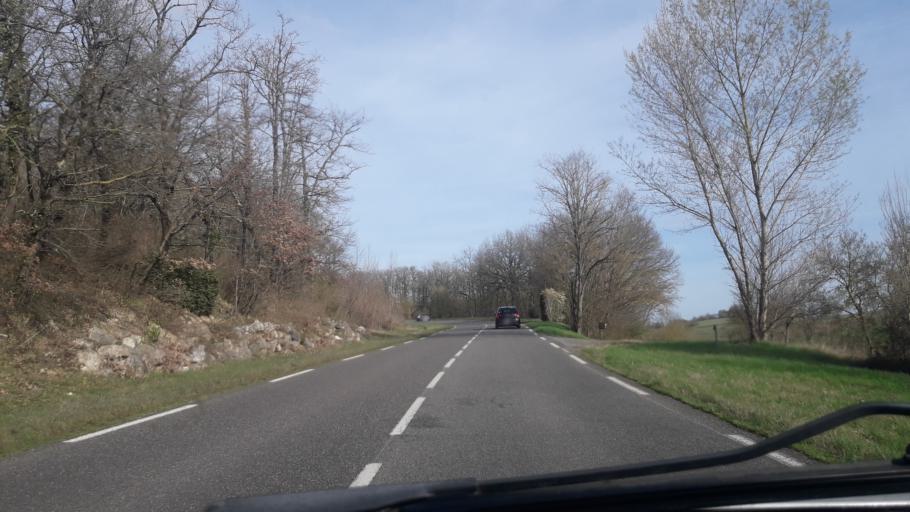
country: FR
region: Midi-Pyrenees
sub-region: Departement du Gers
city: Gimont
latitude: 43.7232
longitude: 0.9613
